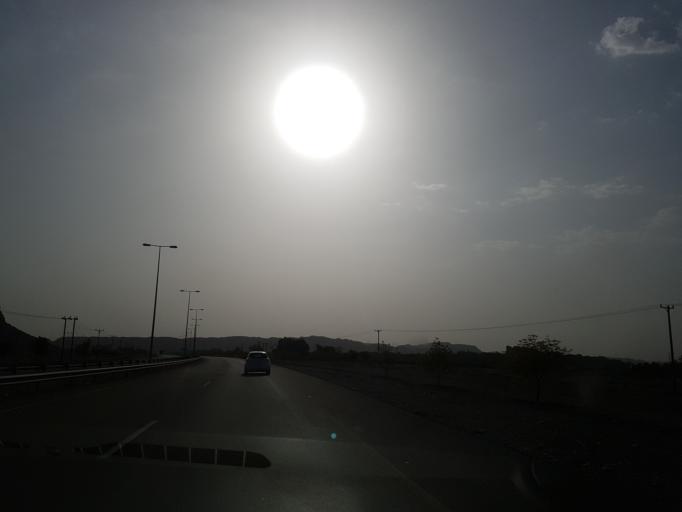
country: OM
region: Al Buraimi
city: Al Buraymi
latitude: 24.2437
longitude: 55.9824
